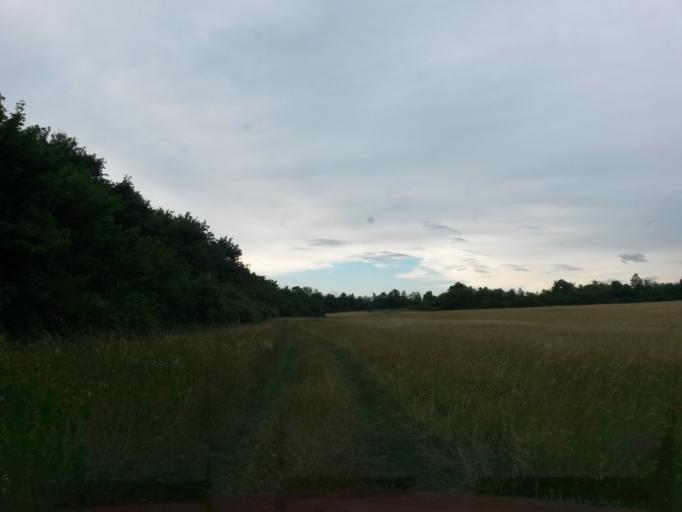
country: SK
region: Banskobystricky
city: Velky Krtis
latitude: 48.3175
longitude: 19.4199
